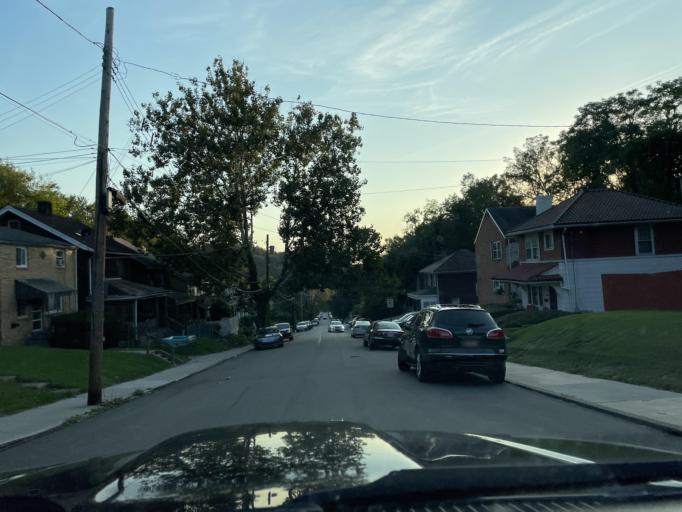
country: US
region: Pennsylvania
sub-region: Allegheny County
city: Wilkinsburg
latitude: 40.4404
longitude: -79.8694
